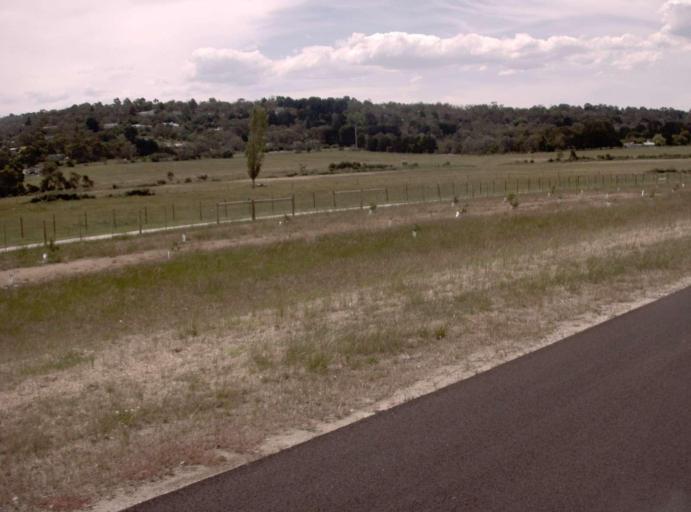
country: AU
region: Victoria
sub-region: Mornington Peninsula
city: Baxter
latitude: -38.2058
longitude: 145.1334
